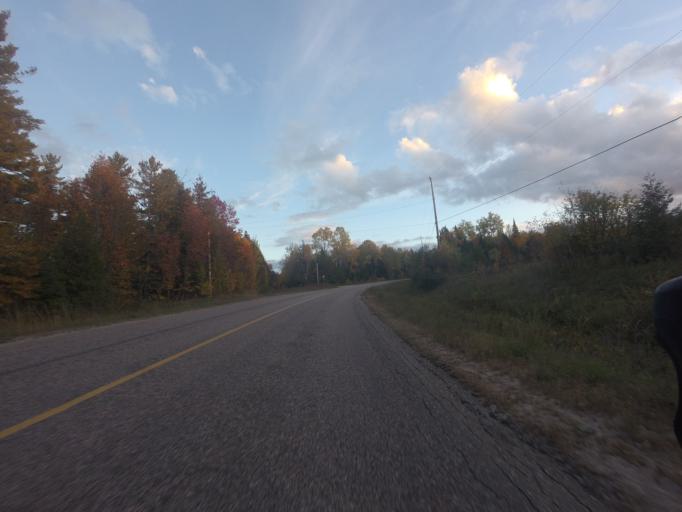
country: CA
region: Ontario
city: Renfrew
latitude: 45.4185
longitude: -76.9521
